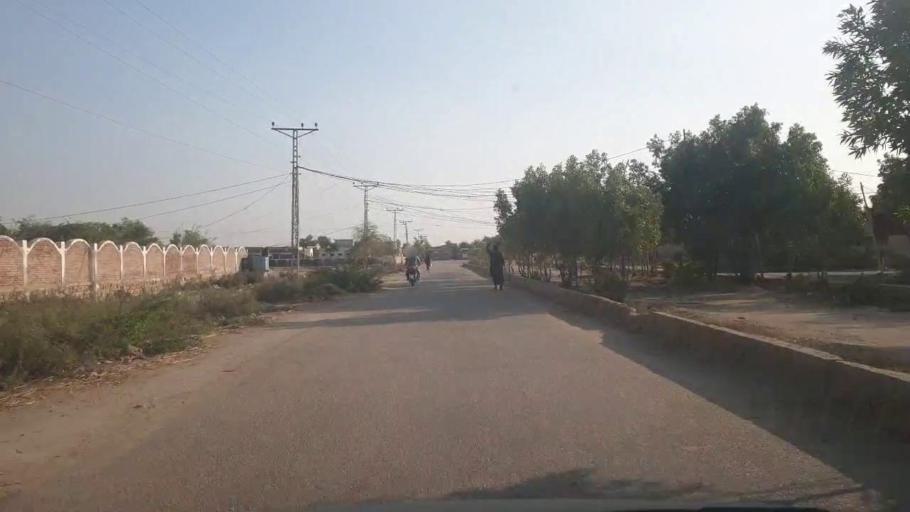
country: PK
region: Sindh
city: Badin
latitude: 24.6537
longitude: 68.8275
